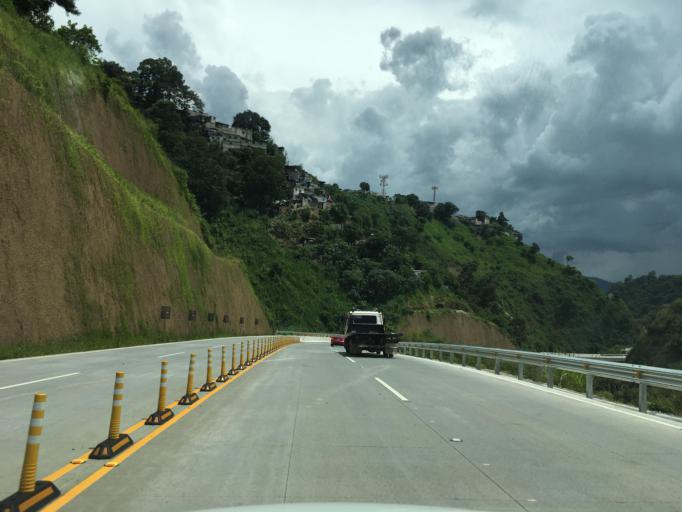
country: GT
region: Guatemala
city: Santa Catarina Pinula
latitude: 14.5614
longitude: -90.5355
